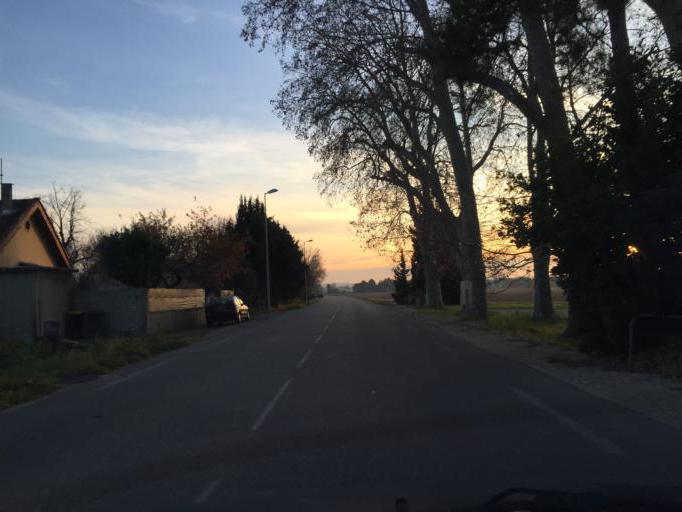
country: FR
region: Provence-Alpes-Cote d'Azur
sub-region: Departement du Vaucluse
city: Jonquieres
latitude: 44.1101
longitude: 4.8946
